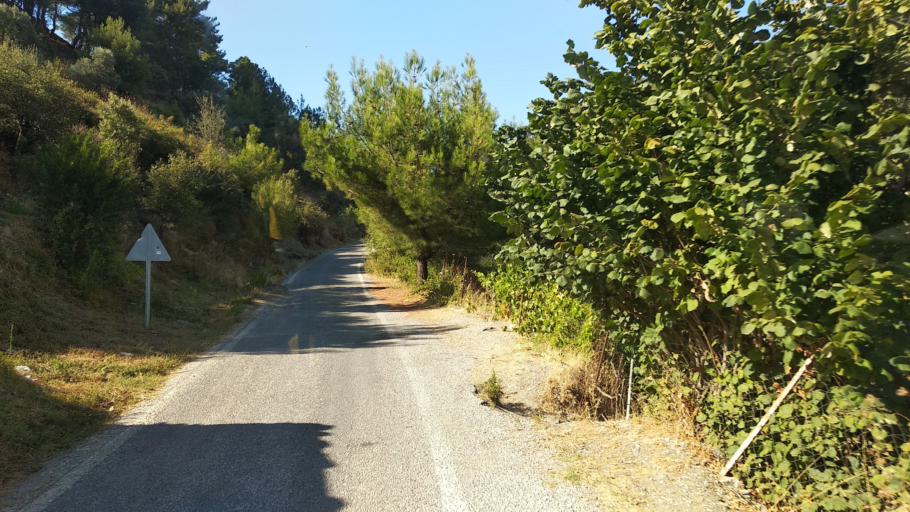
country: TR
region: Izmir
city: Gaziemir
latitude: 38.3250
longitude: 26.9570
